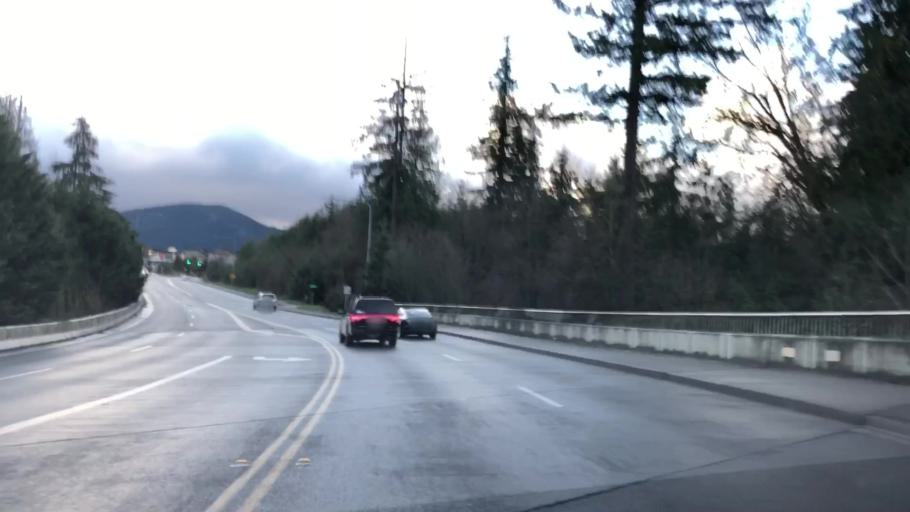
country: US
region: Washington
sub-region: King County
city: Issaquah
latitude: 47.5497
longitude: -122.0229
